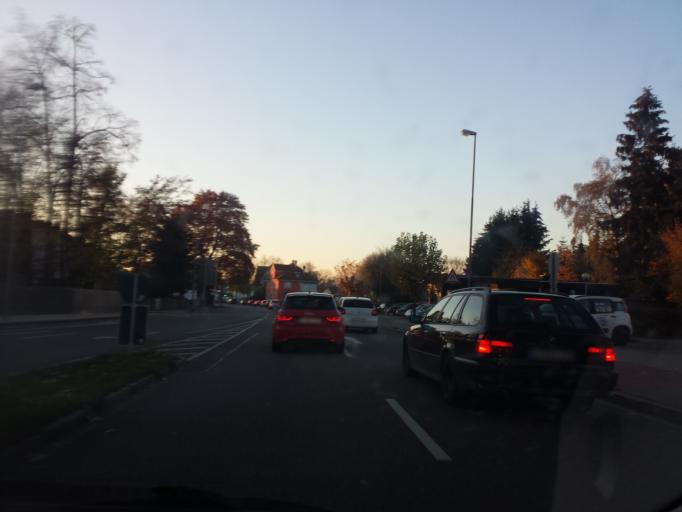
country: DE
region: Bavaria
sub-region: Upper Bavaria
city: Ingolstadt
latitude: 48.7680
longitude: 11.4108
